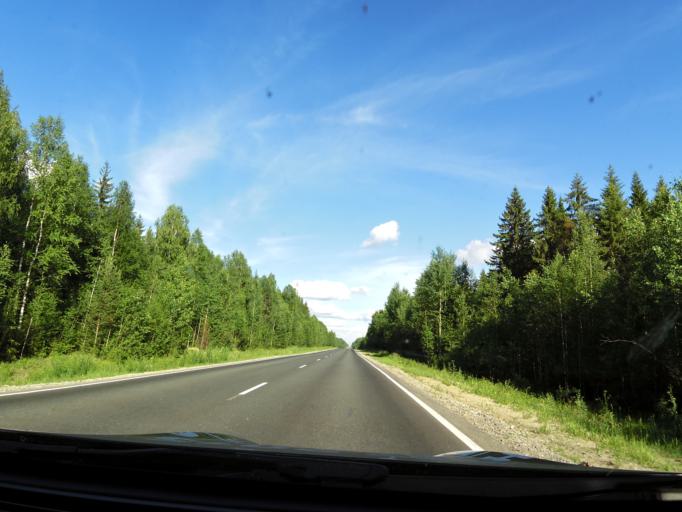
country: RU
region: Kirov
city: Chernaya Kholunitsa
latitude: 58.7748
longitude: 51.9330
